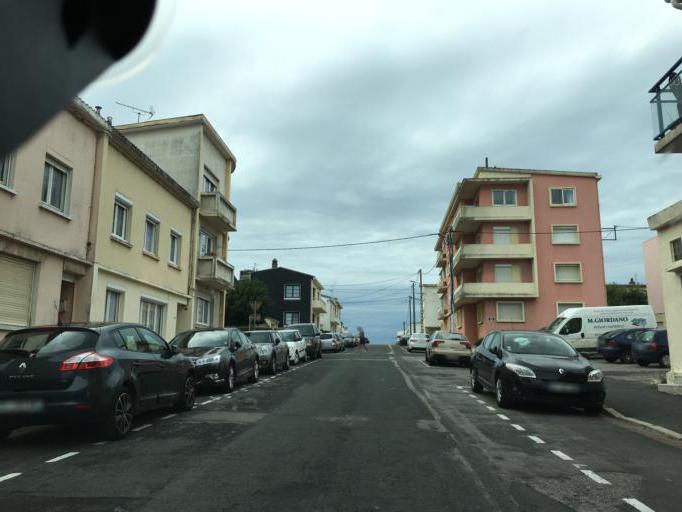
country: FR
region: Nord-Pas-de-Calais
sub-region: Departement du Pas-de-Calais
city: Berck-Plage
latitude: 50.4028
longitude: 1.5612
